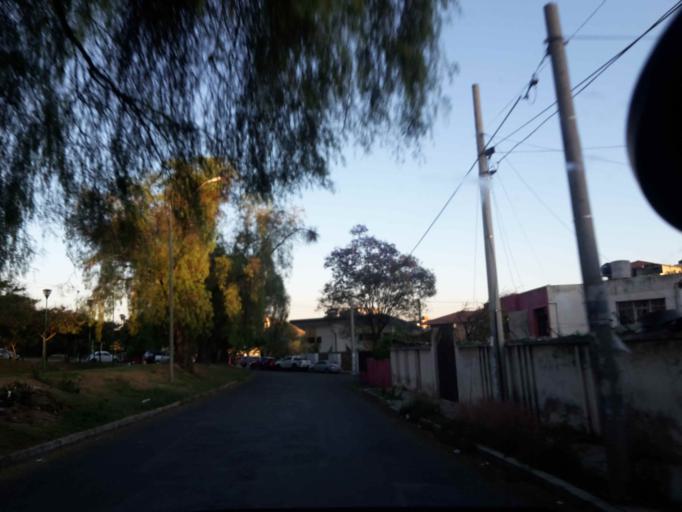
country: BO
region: Cochabamba
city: Cochabamba
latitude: -17.3681
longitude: -66.1598
